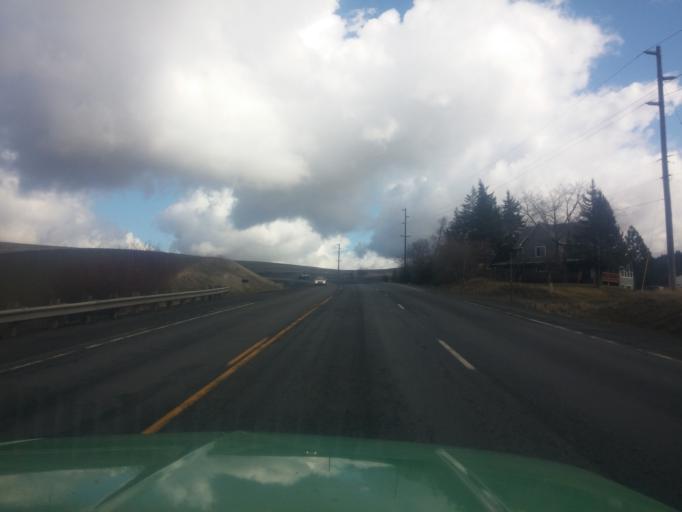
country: US
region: Idaho
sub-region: Latah County
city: Moscow
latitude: 46.8619
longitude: -117.0140
